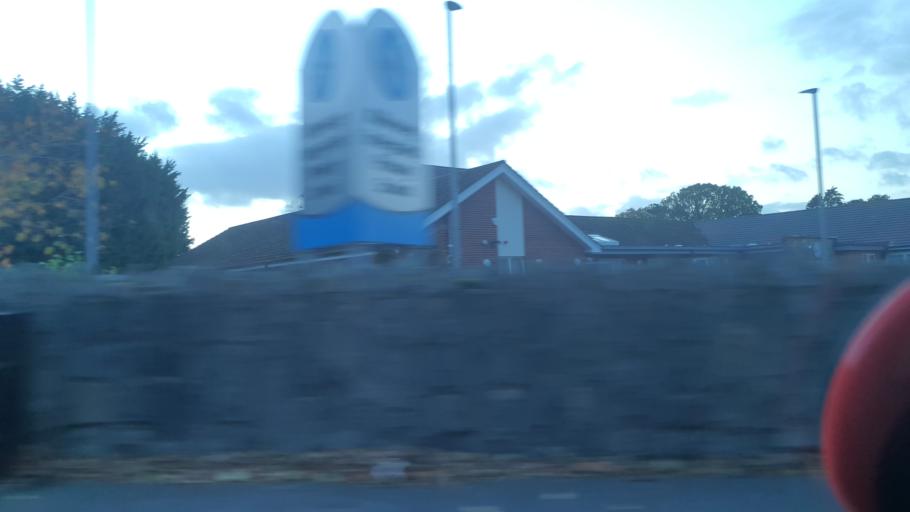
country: GB
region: Northern Ireland
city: Rostrevor
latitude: 54.0990
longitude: -6.1948
